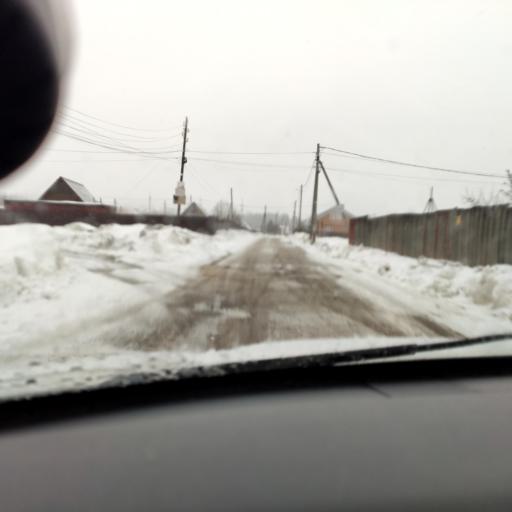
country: RU
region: Perm
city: Polazna
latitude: 58.1797
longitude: 56.4023
